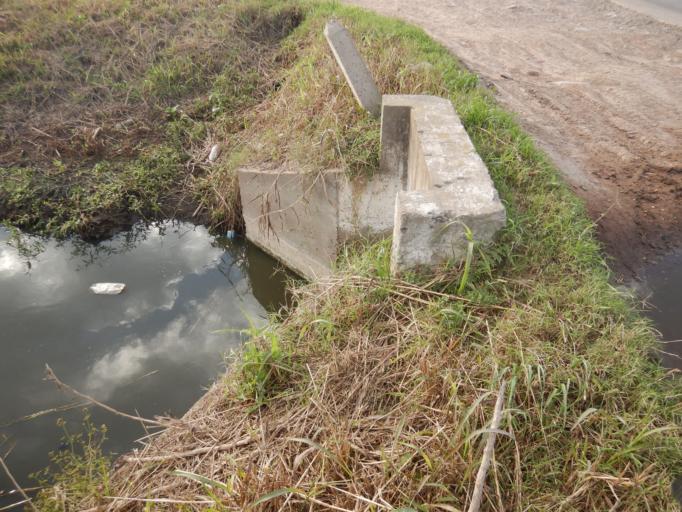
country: AR
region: Santa Fe
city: Roldan
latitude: -32.8981
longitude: -60.9497
